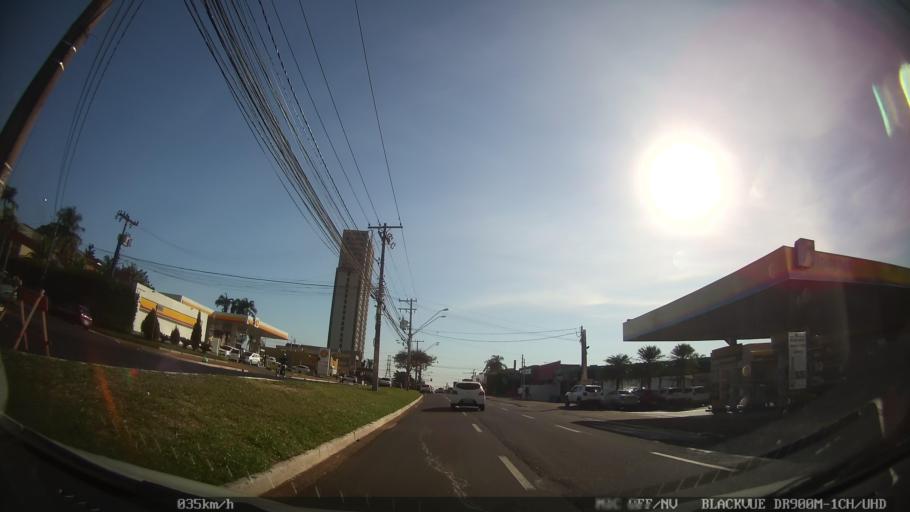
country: BR
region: Sao Paulo
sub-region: Ribeirao Preto
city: Ribeirao Preto
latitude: -21.1993
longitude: -47.8081
